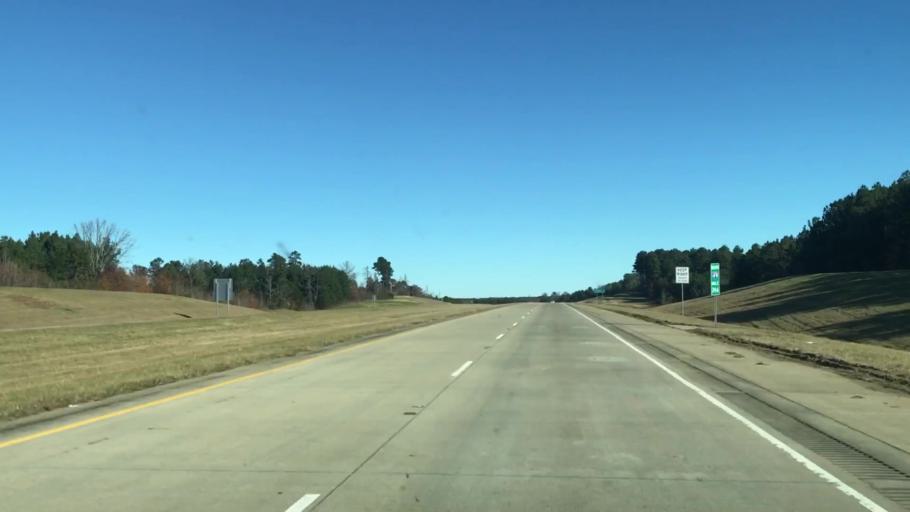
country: US
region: Louisiana
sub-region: Caddo Parish
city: Vivian
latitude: 33.0095
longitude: -93.9043
